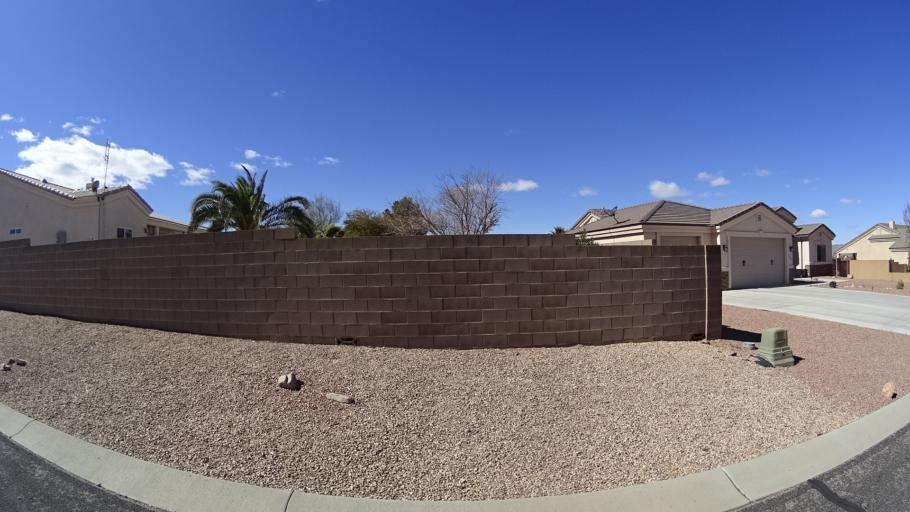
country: US
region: Arizona
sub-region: Mohave County
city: New Kingman-Butler
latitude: 35.2081
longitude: -113.9714
